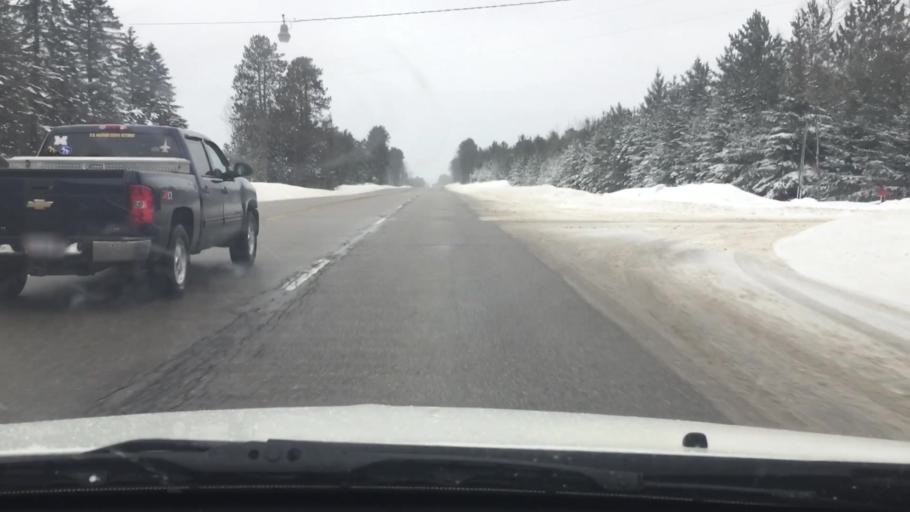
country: US
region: Michigan
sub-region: Otsego County
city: Gaylord
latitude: 45.0427
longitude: -84.7758
